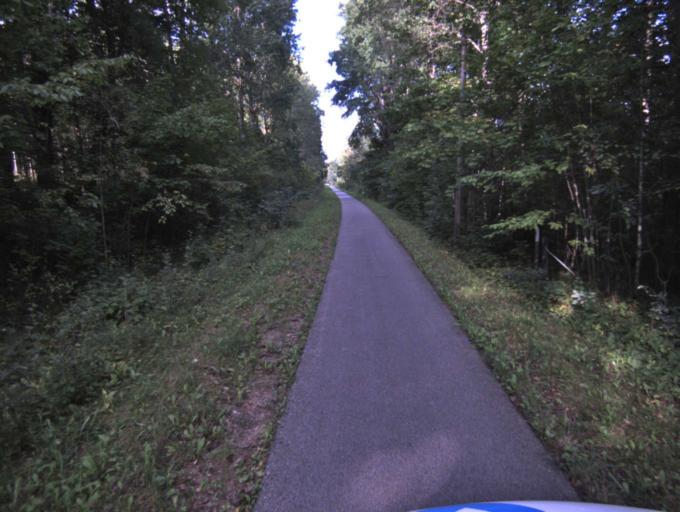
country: SE
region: Vaestra Goetaland
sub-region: Ulricehamns Kommun
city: Ulricehamn
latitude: 57.9054
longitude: 13.4710
